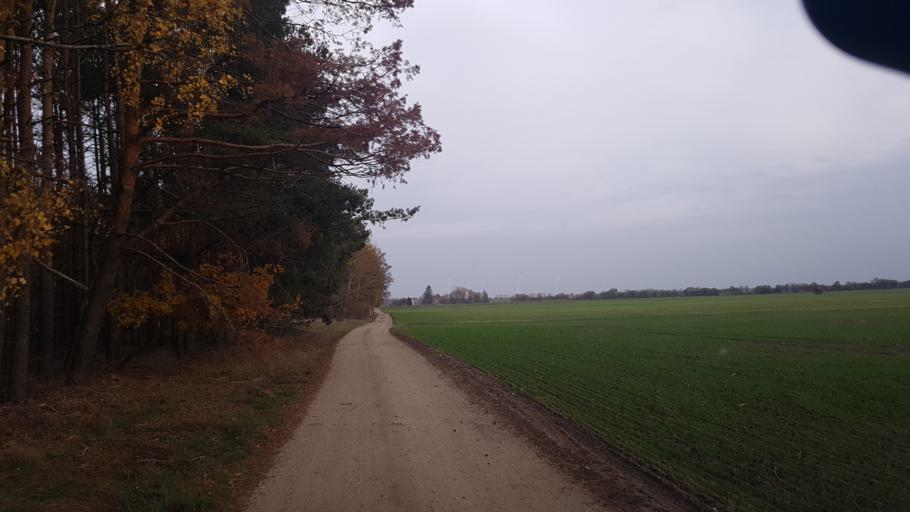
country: DE
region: Brandenburg
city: Schilda
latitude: 51.6572
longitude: 13.3994
